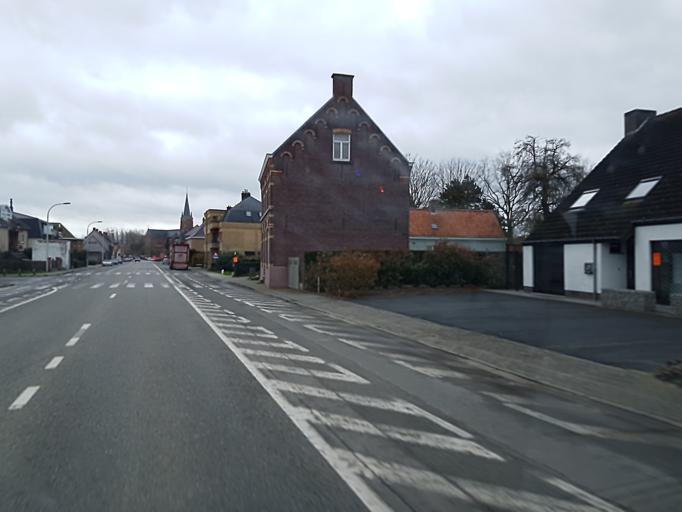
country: BE
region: Flanders
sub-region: Provincie Oost-Vlaanderen
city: De Pinte
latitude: 50.9582
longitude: 3.6368
